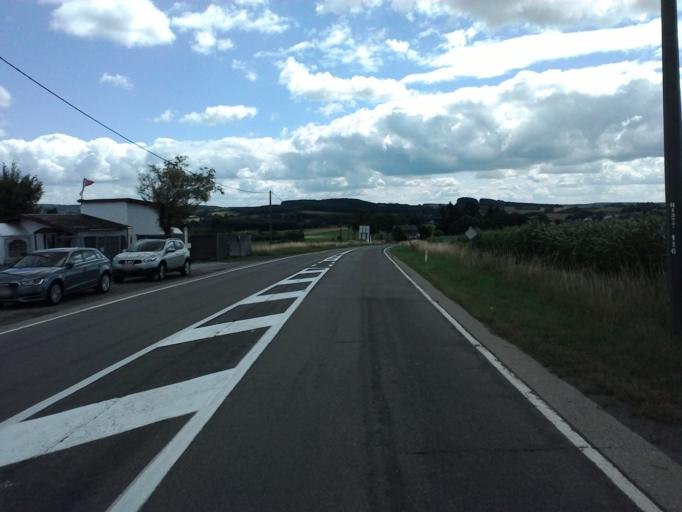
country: BE
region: Wallonia
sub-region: Province du Luxembourg
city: Leglise
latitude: 49.8078
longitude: 5.5206
